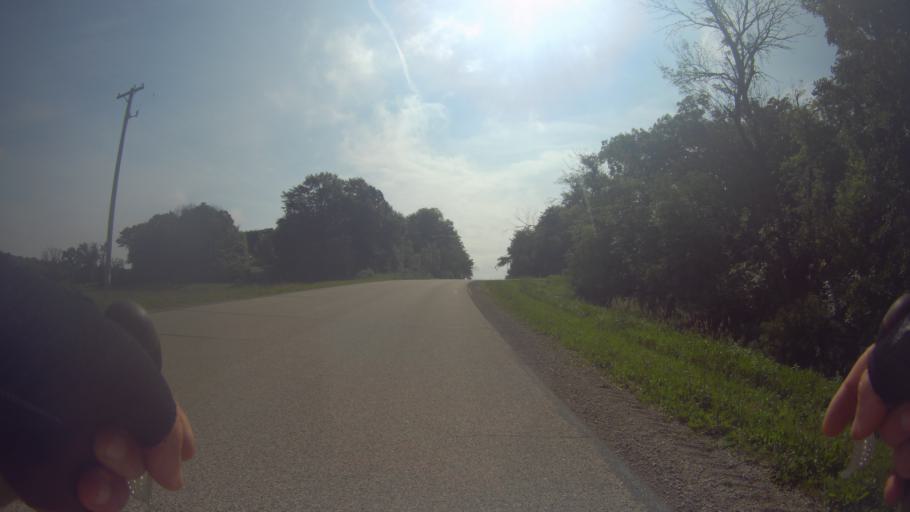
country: US
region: Wisconsin
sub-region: Dane County
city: Stoughton
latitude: 42.9920
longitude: -89.1917
